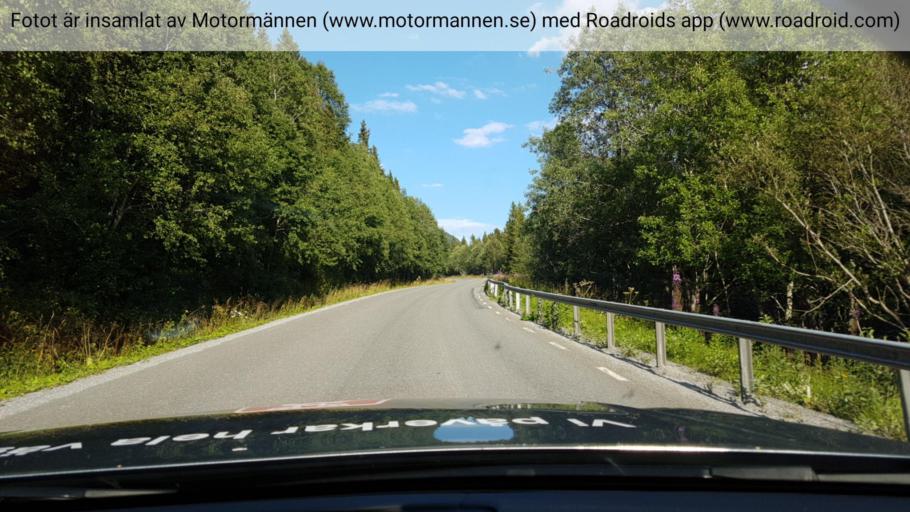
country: SE
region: Jaemtland
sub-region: Are Kommun
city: Are
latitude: 63.4096
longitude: 13.0375
